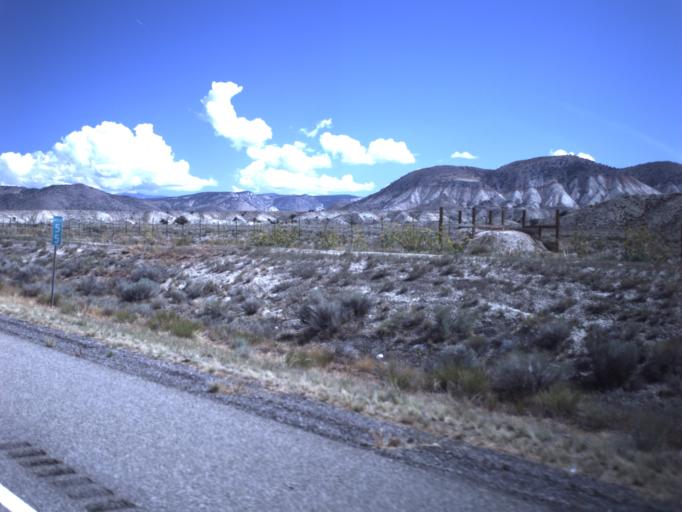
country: US
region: Utah
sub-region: Sevier County
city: Salina
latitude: 38.9187
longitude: -111.8790
